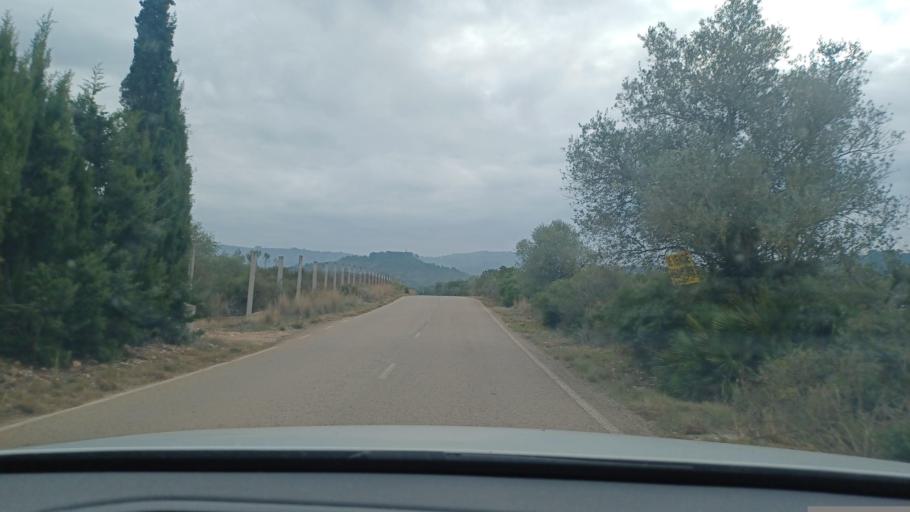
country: ES
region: Catalonia
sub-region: Provincia de Tarragona
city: Santa Barbara
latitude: 40.6633
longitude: 0.4574
